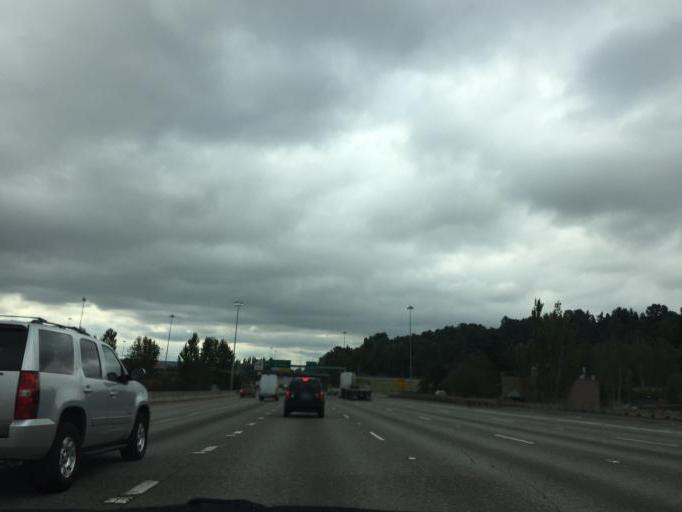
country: US
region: Washington
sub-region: King County
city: Tukwila
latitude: 47.4662
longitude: -122.2673
